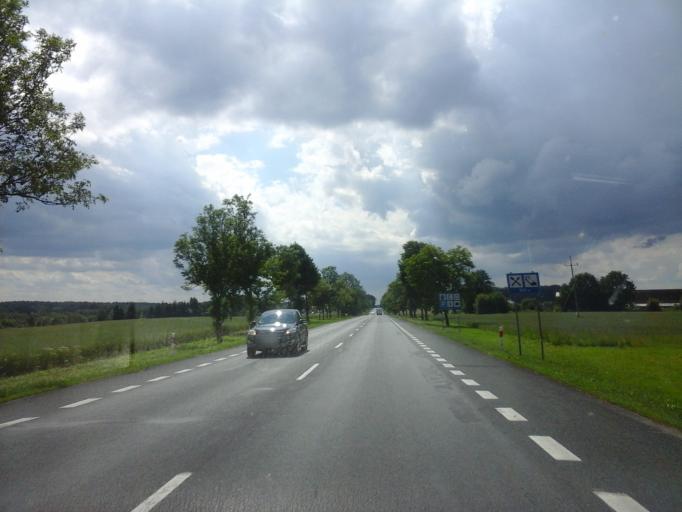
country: PL
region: West Pomeranian Voivodeship
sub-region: Powiat bialogardzki
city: Karlino
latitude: 54.0587
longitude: 15.9298
